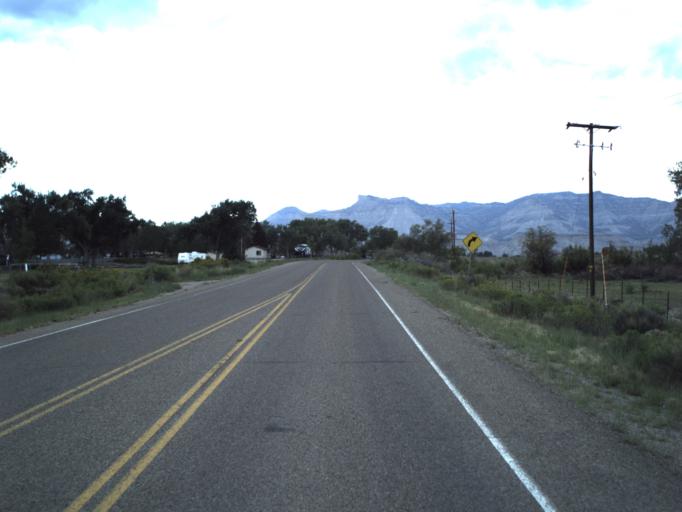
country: US
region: Utah
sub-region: Emery County
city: Huntington
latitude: 39.3459
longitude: -110.9402
